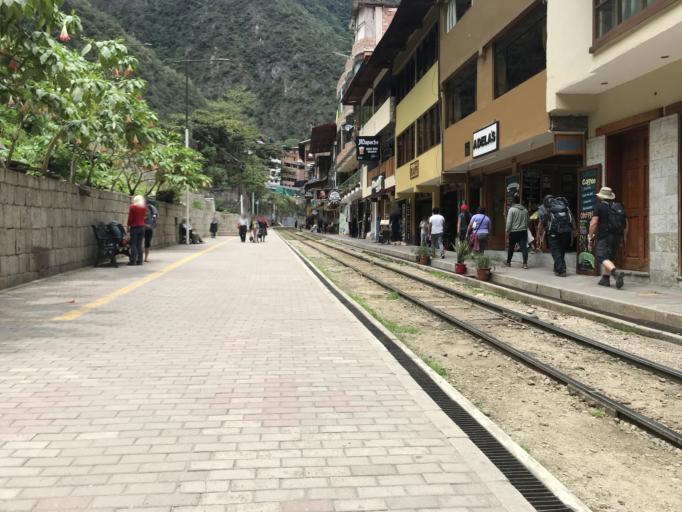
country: PE
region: Cusco
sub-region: Provincia de La Convencion
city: Santa Teresa
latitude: -13.1554
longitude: -72.5252
